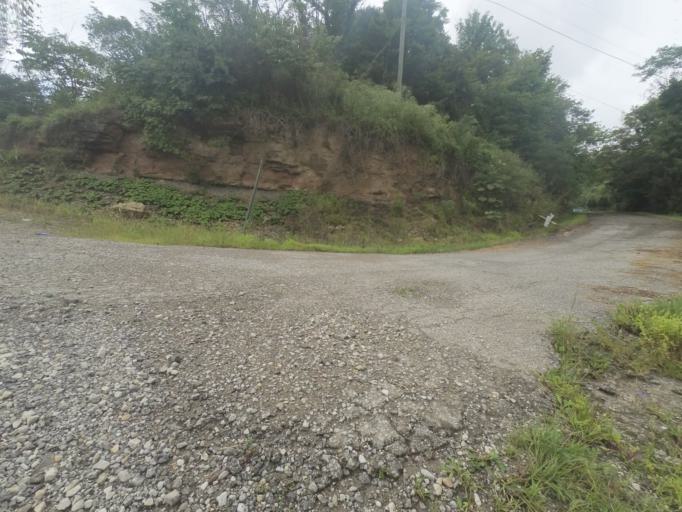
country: US
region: West Virginia
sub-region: Cabell County
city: Huntington
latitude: 38.4273
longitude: -82.4733
